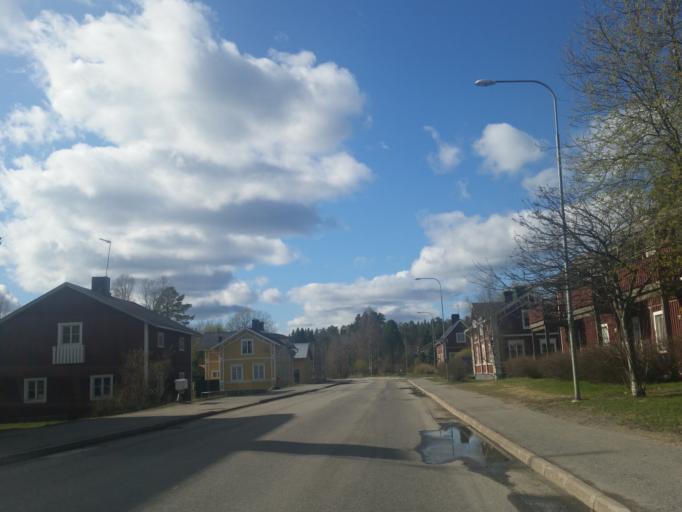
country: SE
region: Vaesterbotten
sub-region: Robertsfors Kommun
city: Robertsfors
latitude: 64.1951
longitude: 20.8441
